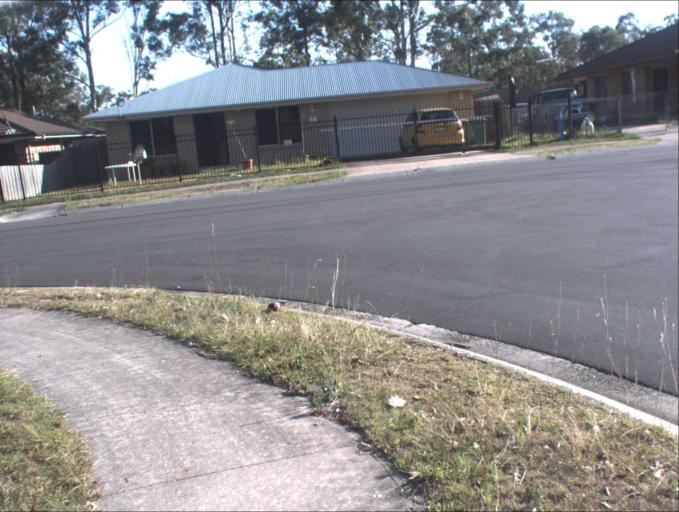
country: AU
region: Queensland
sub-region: Logan
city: Logan City
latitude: -27.6597
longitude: 153.0941
